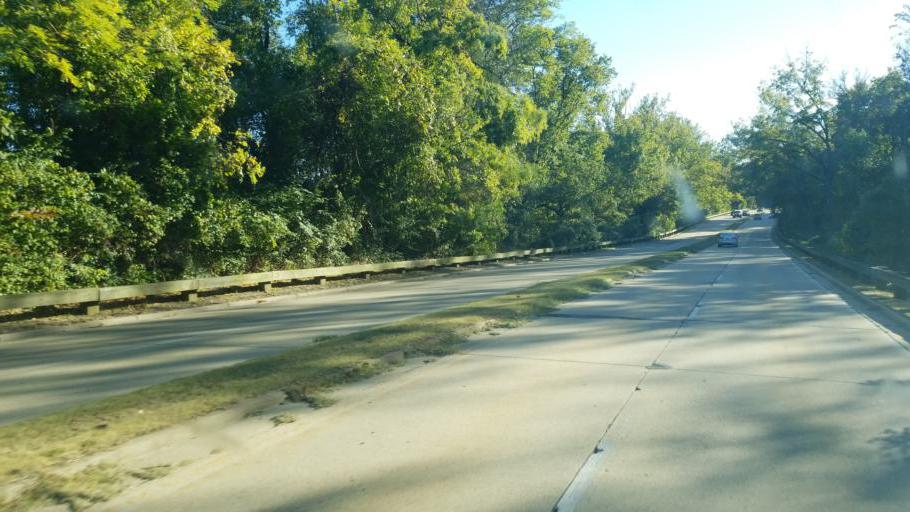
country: US
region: Virginia
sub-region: Fairfax County
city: Fort Hunt
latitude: 38.7163
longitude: -77.0457
